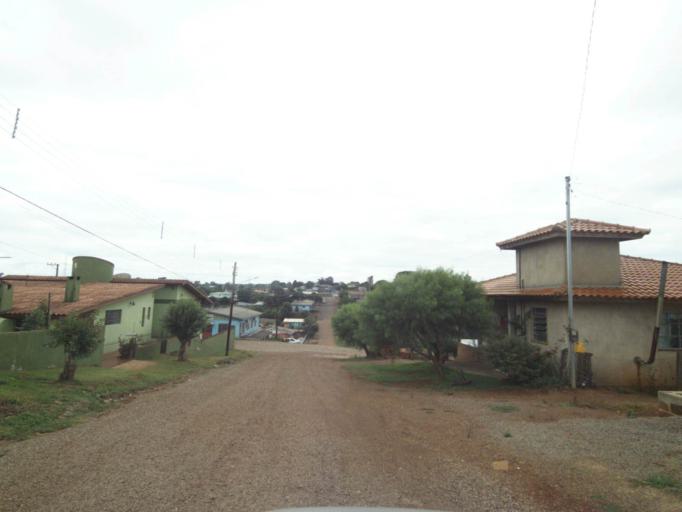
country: BR
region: Rio Grande do Sul
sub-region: Lagoa Vermelha
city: Lagoa Vermelha
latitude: -28.2182
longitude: -51.5372
